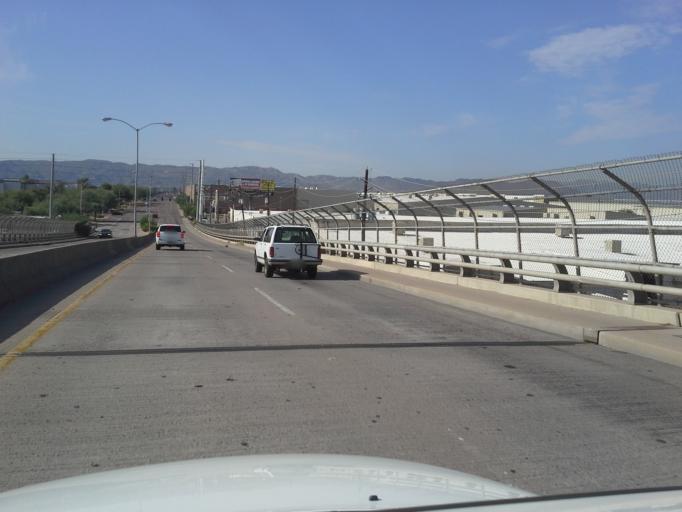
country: US
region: Arizona
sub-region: Maricopa County
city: Phoenix
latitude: 33.4438
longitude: -112.0478
